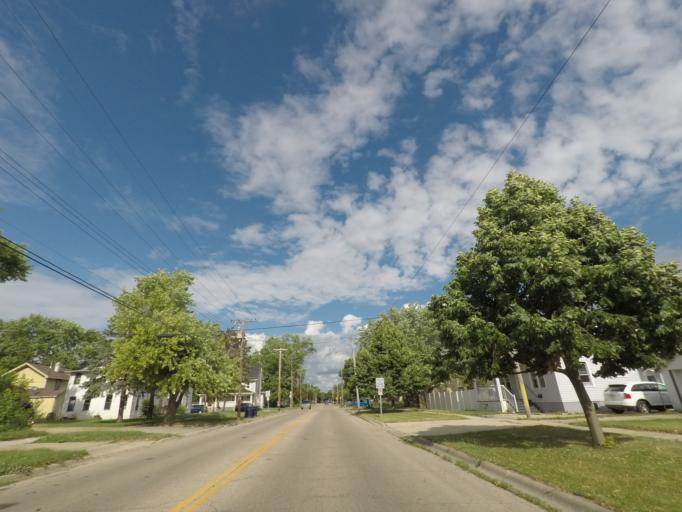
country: US
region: Wisconsin
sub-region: Rock County
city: Janesville
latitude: 42.6742
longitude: -89.0266
